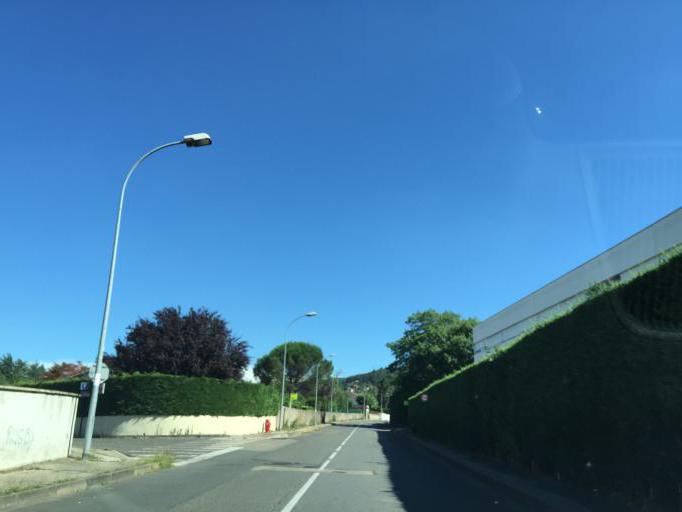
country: FR
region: Rhone-Alpes
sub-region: Departement de la Loire
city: Saint-Chamond
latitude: 45.4701
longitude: 4.5202
